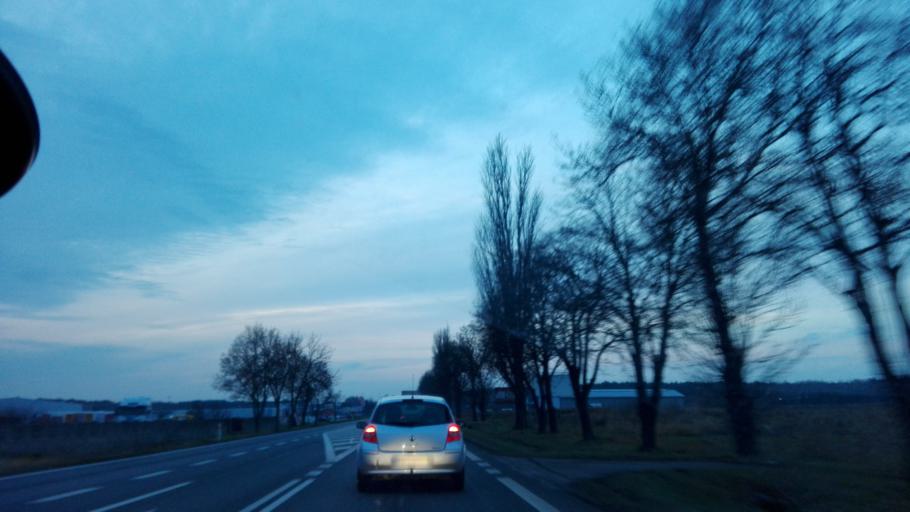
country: PL
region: Masovian Voivodeship
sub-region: Powiat siedlecki
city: Skorzec
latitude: 52.1792
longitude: 22.1707
